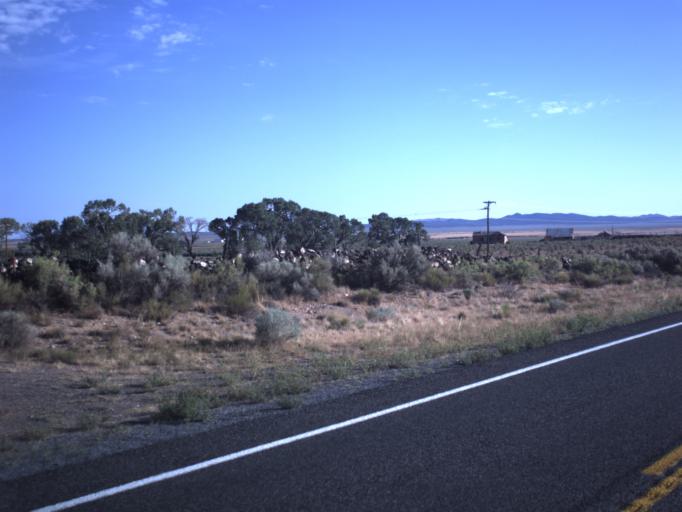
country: US
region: Utah
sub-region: Iron County
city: Enoch
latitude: 37.8544
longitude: -113.0326
